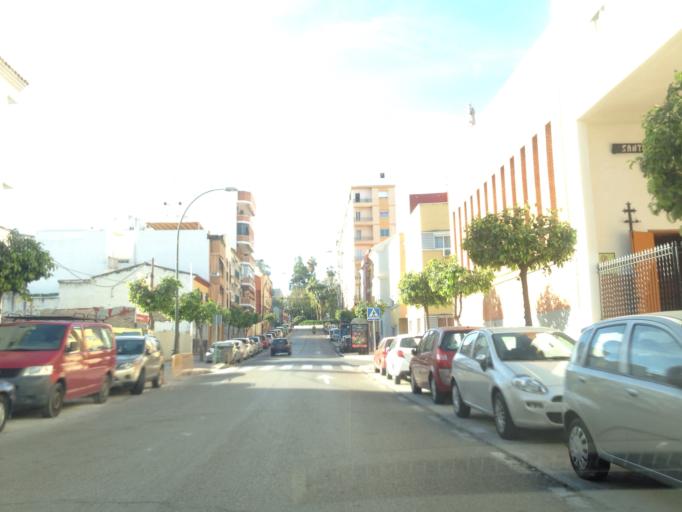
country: ES
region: Andalusia
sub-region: Provincia de Malaga
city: Malaga
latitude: 36.7309
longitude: -4.4215
